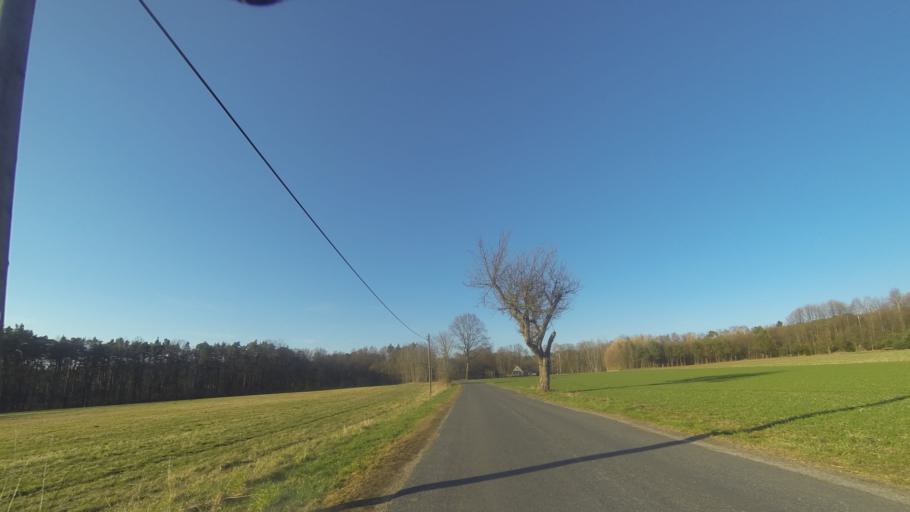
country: DE
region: Saxony
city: Ottendorf-Okrilla
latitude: 51.1925
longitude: 13.7953
